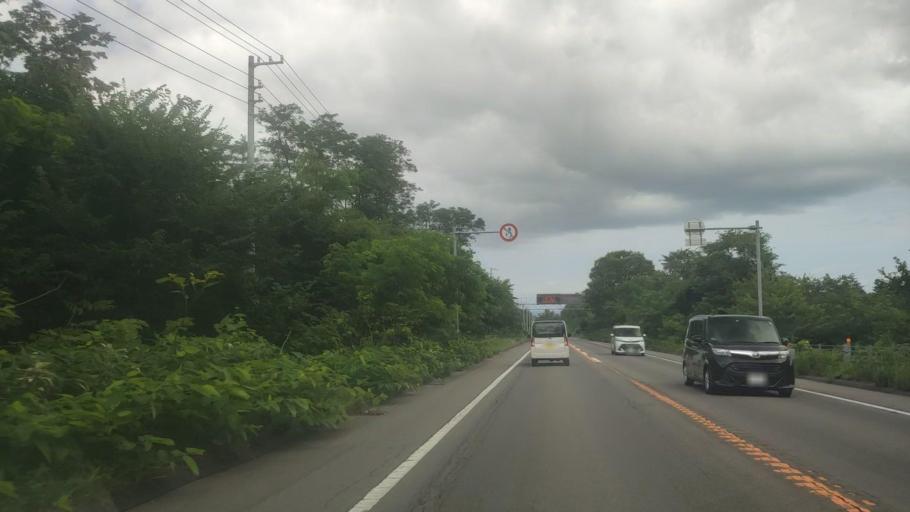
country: JP
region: Hokkaido
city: Nanae
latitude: 42.0730
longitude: 140.6020
